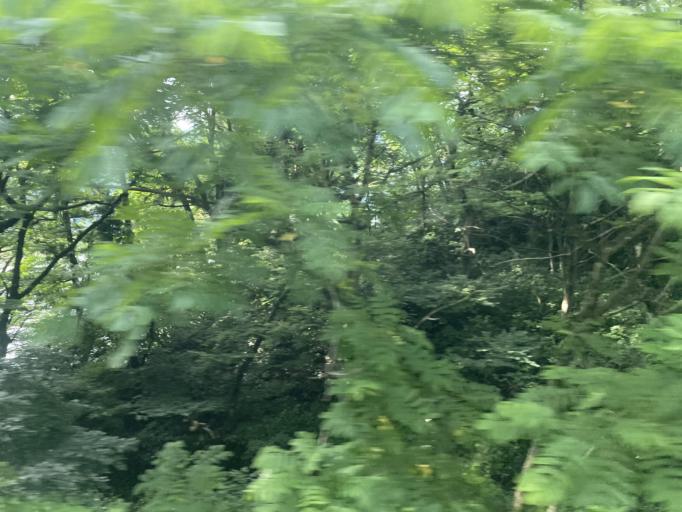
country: JP
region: Niigata
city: Suibara
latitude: 37.7359
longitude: 139.3110
